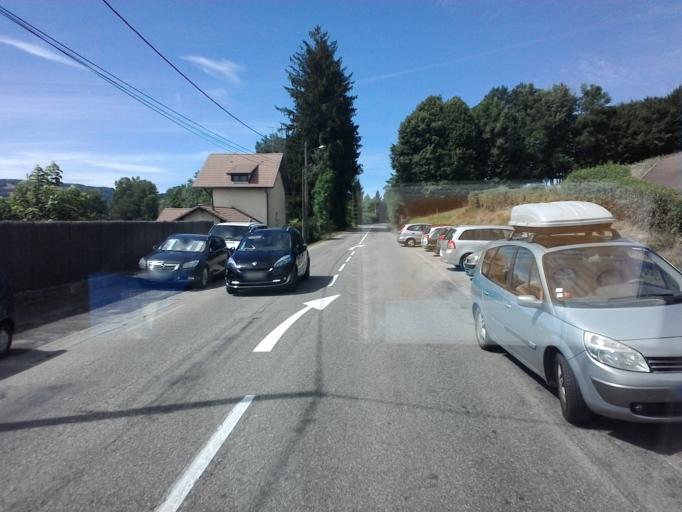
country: FR
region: Rhone-Alpes
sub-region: Departement de l'Isere
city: Le Pin
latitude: 45.4522
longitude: 5.5221
